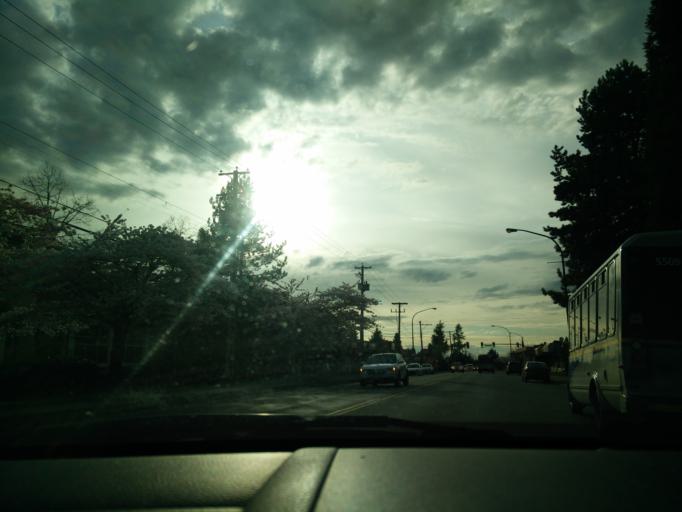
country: CA
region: British Columbia
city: Burnaby
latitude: 49.2150
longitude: -122.9866
